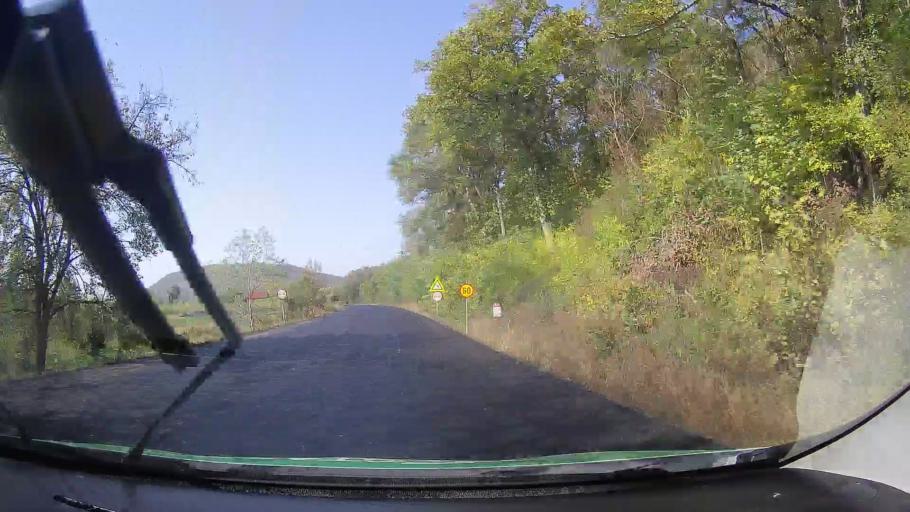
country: RO
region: Arad
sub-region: Comuna Petris
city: Petris
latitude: 46.0183
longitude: 22.4116
